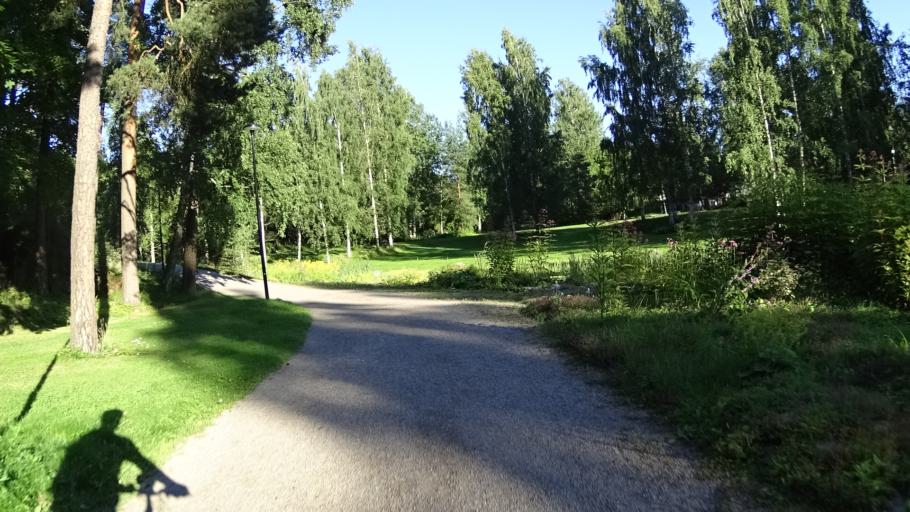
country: FI
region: Uusimaa
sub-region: Helsinki
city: Helsinki
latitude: 60.1866
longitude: 24.8966
